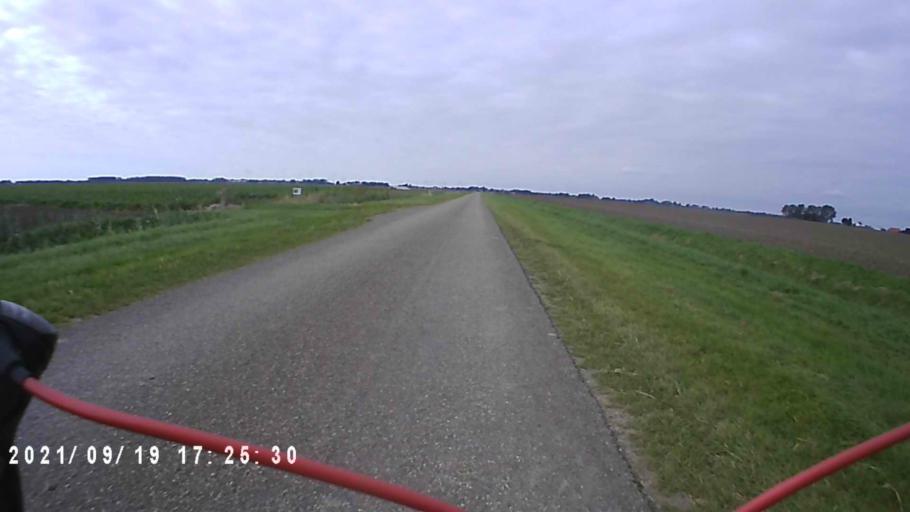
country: NL
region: Groningen
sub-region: Gemeente  Oldambt
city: Winschoten
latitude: 53.2218
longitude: 7.0131
